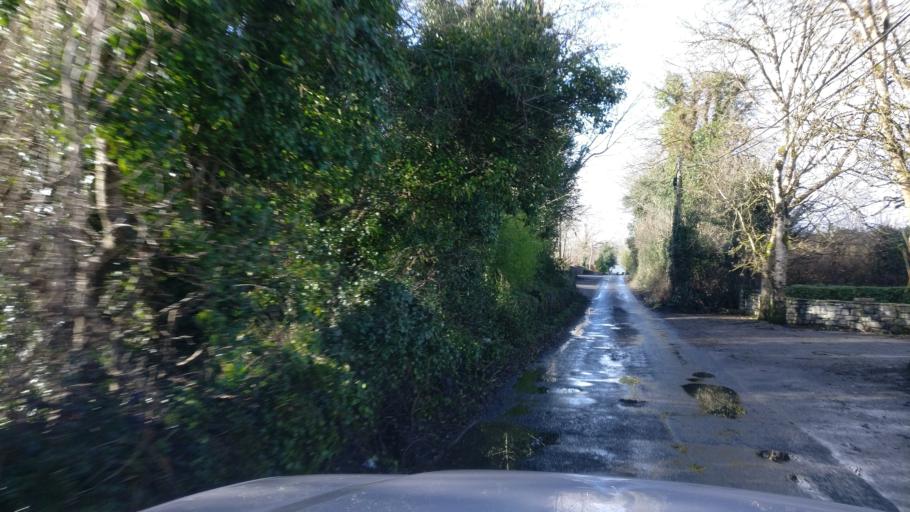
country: IE
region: Connaught
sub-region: County Galway
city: Athenry
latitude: 53.2274
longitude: -8.7409
